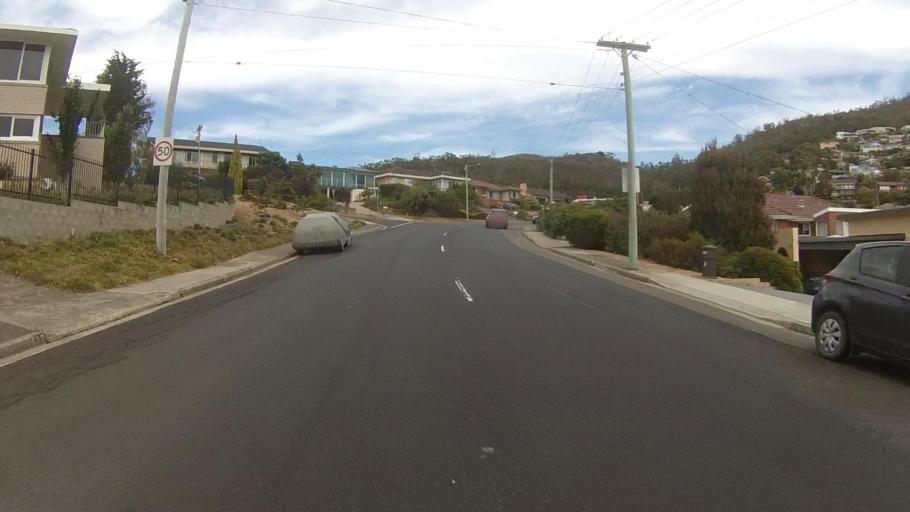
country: AU
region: Tasmania
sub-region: Kingborough
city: Taroona
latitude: -42.9181
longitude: 147.3556
